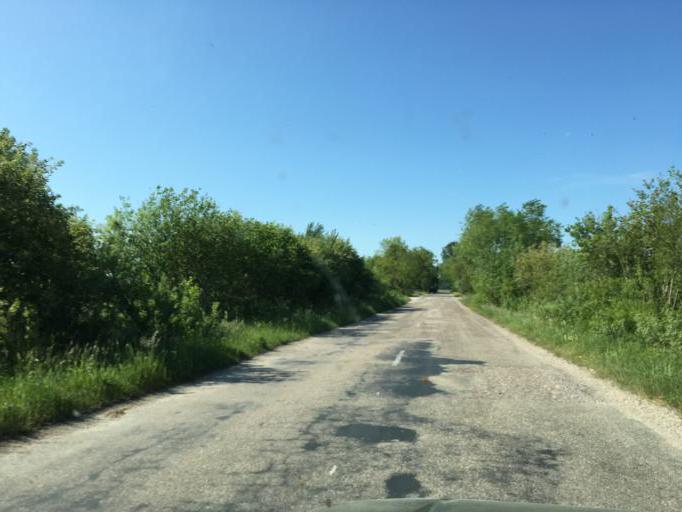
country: LV
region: Ventspils
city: Ventspils
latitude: 57.5018
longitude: 21.8445
